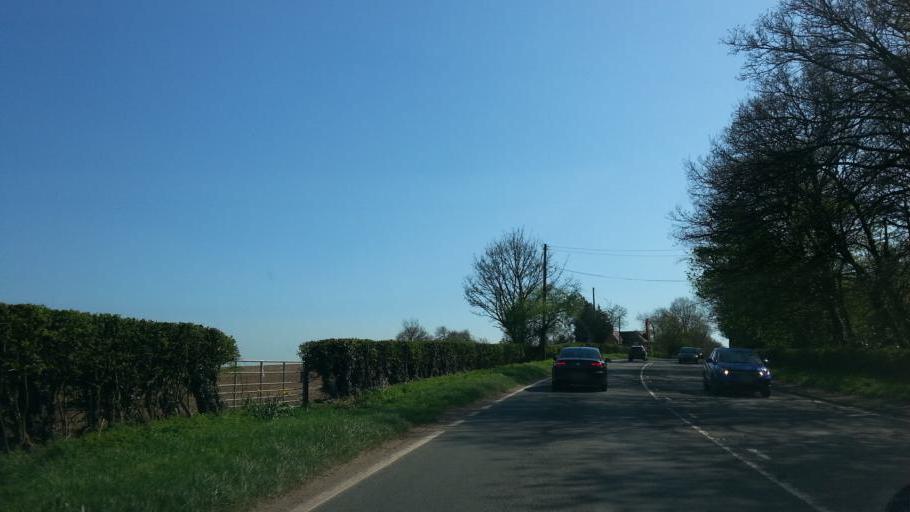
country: GB
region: England
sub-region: Worcestershire
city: Alvechurch
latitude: 52.3840
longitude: -1.9575
